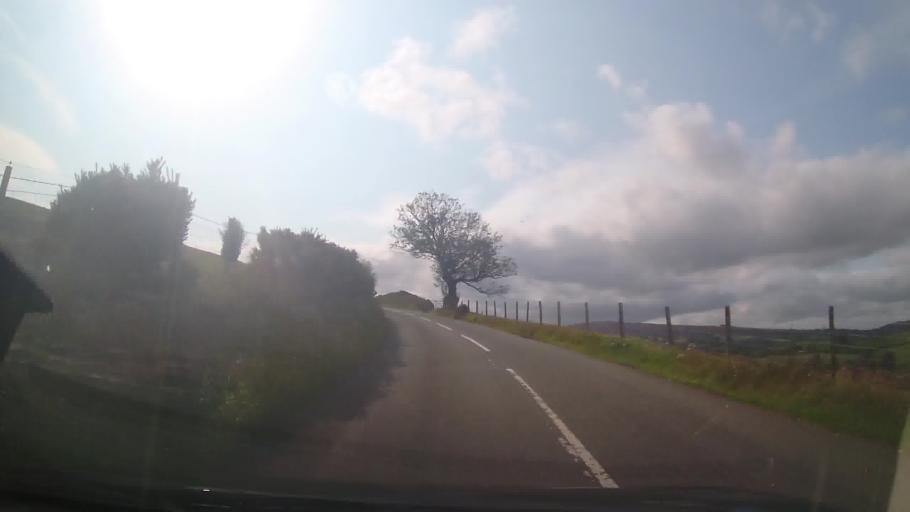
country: GB
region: England
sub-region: Shropshire
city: Pontesbury
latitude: 52.6040
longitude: -2.8678
